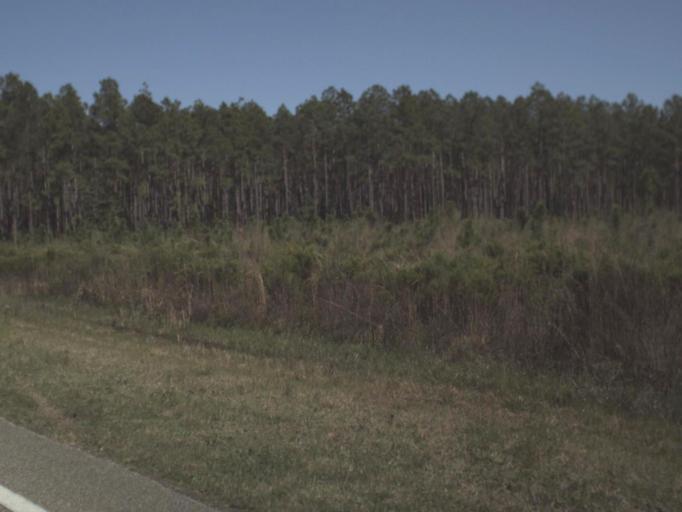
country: US
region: Florida
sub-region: Gulf County
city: Port Saint Joe
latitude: 29.8369
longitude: -85.2737
